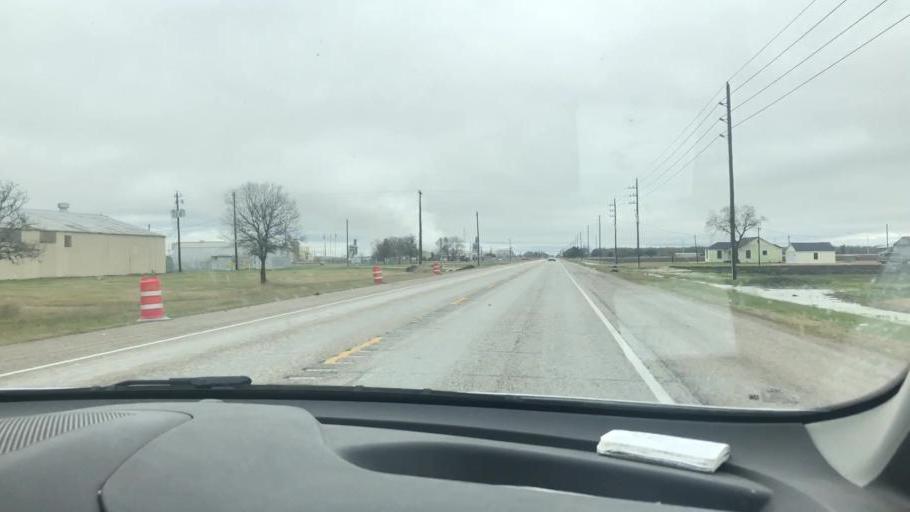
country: US
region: Texas
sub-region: Wharton County
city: Wharton
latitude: 29.2985
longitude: -96.0772
